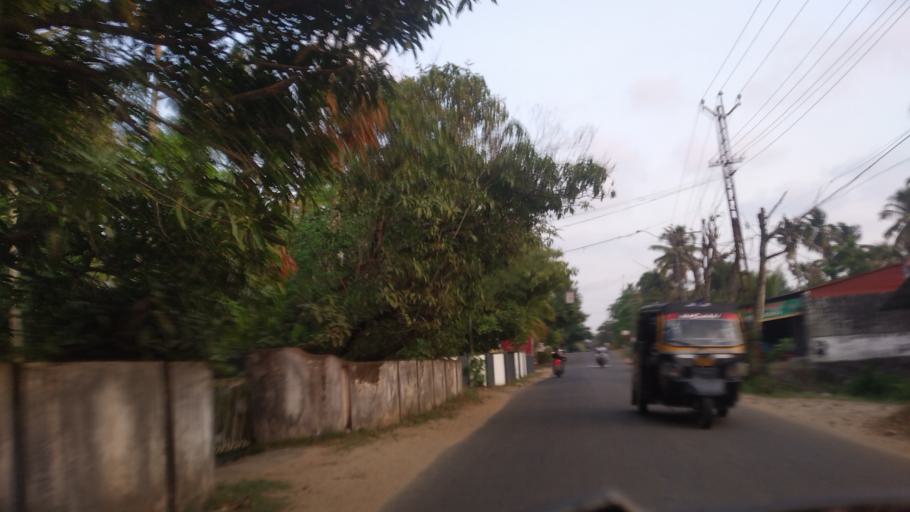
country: IN
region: Kerala
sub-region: Thrissur District
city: Kodungallur
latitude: 10.2273
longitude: 76.1555
